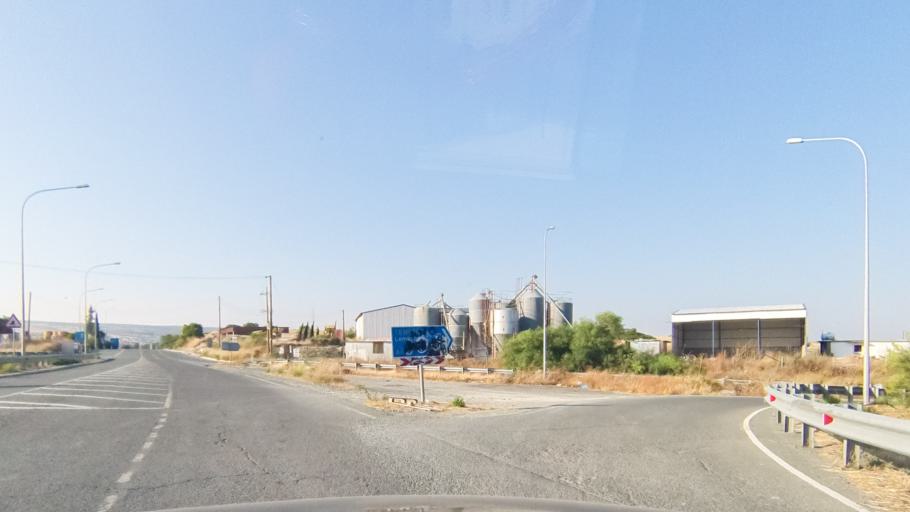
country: CY
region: Limassol
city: Pissouri
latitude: 34.6834
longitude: 32.7606
